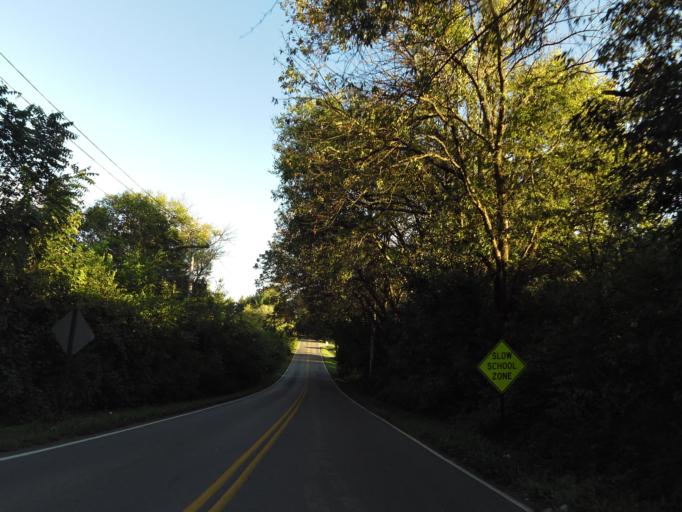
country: US
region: Tennessee
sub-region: Blount County
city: Eagleton Village
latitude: 35.8263
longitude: -83.9459
